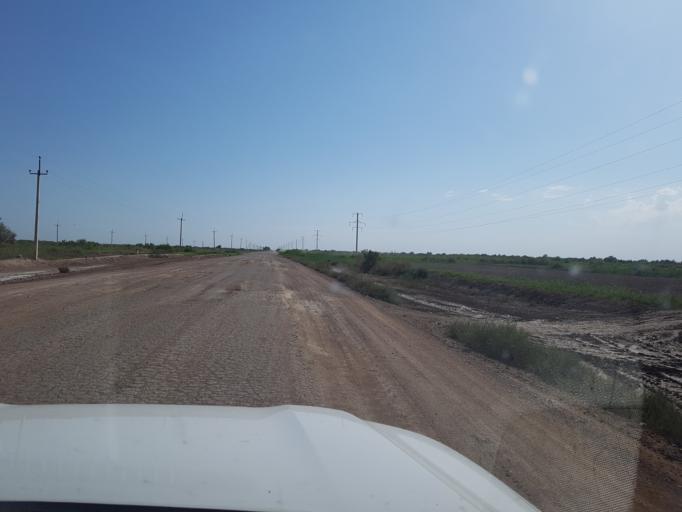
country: TM
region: Dasoguz
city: Koeneuergench
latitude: 42.1192
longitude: 58.9295
